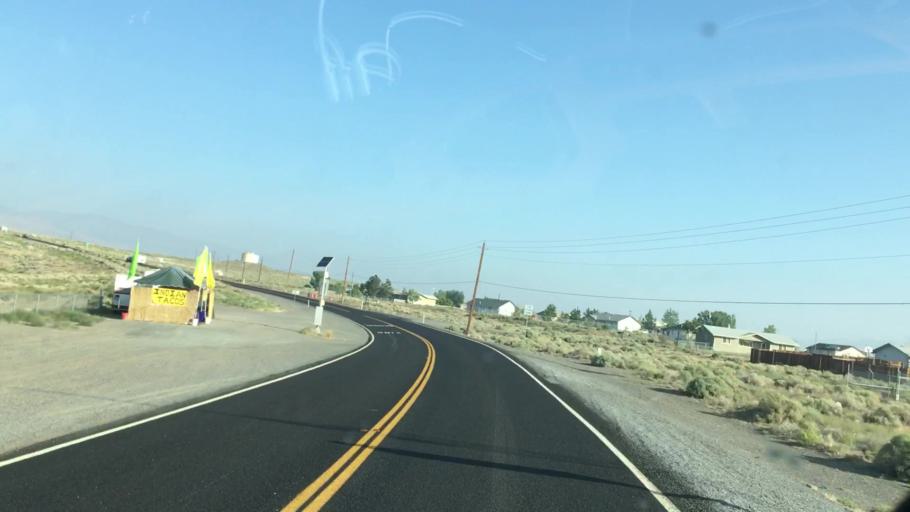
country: US
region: Nevada
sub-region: Lyon County
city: Fernley
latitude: 39.6369
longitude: -119.2909
